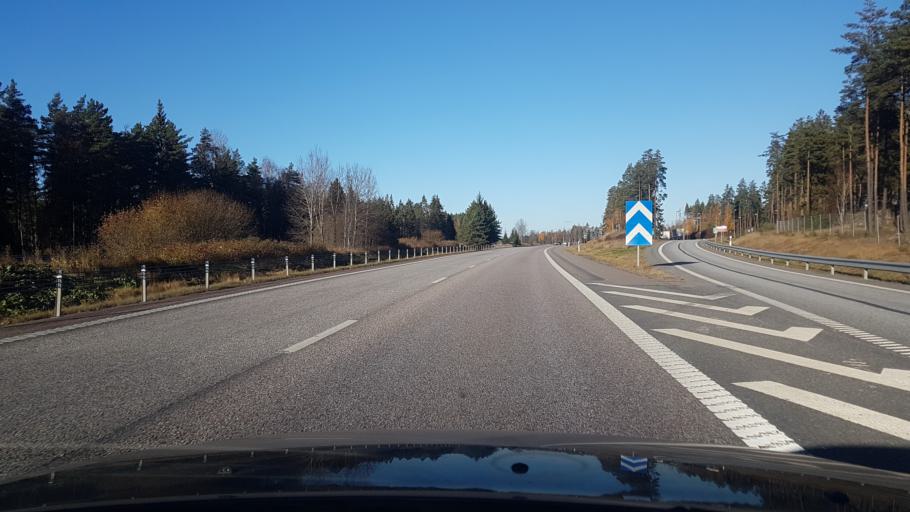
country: SE
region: Uppsala
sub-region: Uppsala Kommun
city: Alsike
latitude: 59.7910
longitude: 17.7749
